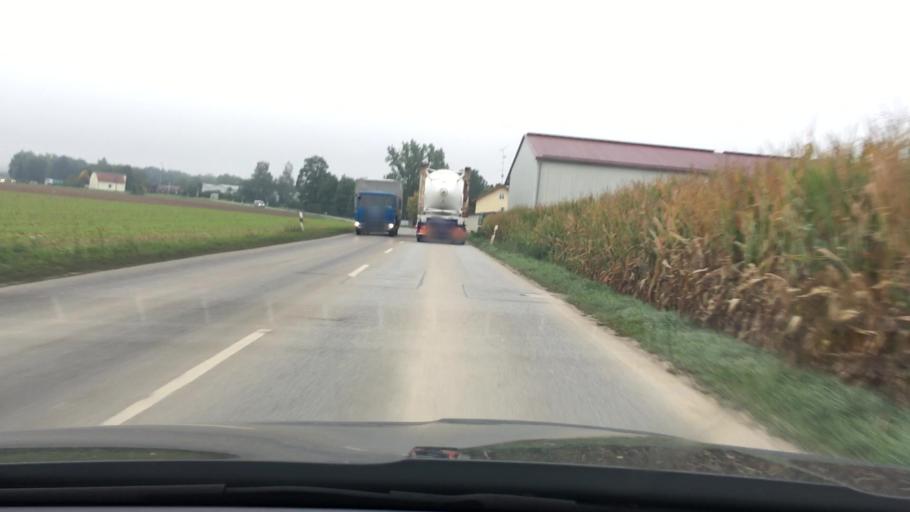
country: DE
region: Bavaria
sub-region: Lower Bavaria
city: Plattling
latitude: 48.7950
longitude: 12.8840
